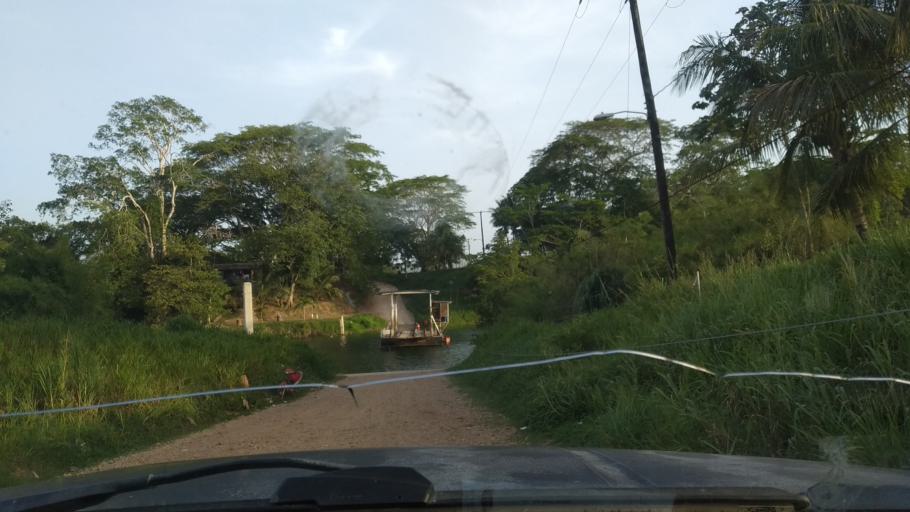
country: BZ
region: Cayo
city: San Ignacio
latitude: 17.2061
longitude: -89.0139
